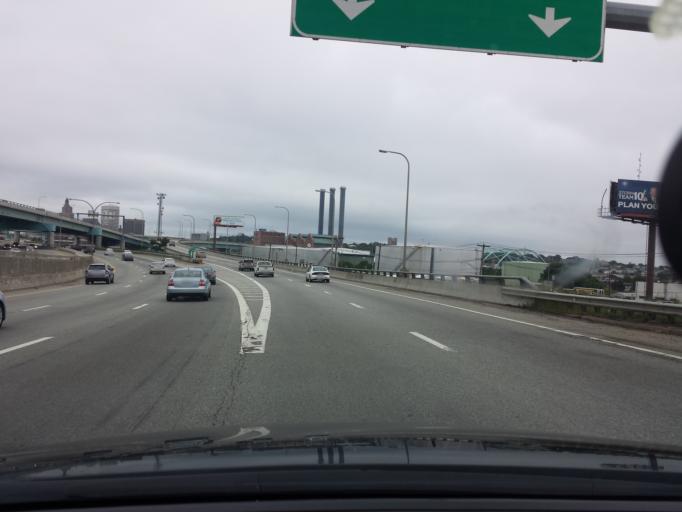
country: US
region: Rhode Island
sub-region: Providence County
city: Providence
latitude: 41.8091
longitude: -71.4046
